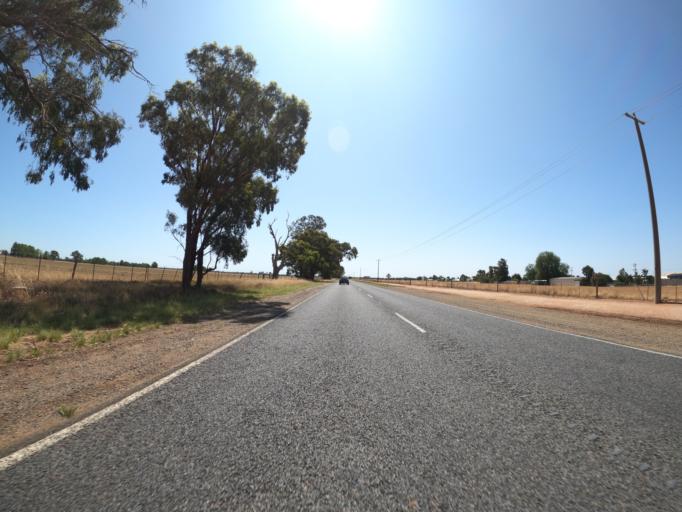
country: AU
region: Victoria
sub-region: Moira
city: Yarrawonga
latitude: -36.0247
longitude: 146.0656
